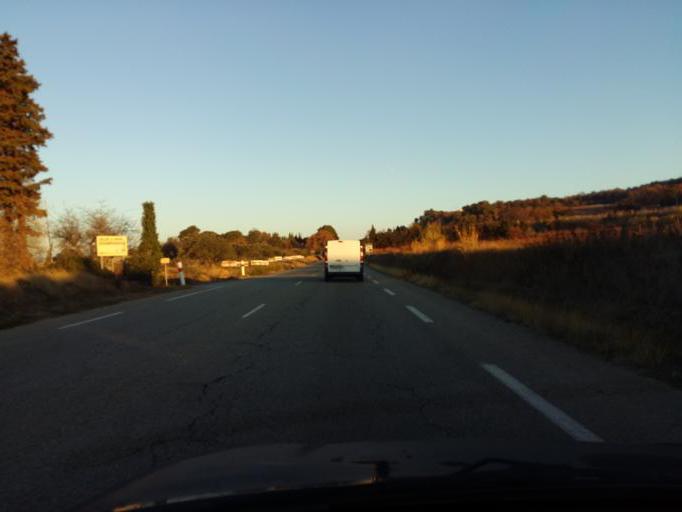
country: FR
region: Provence-Alpes-Cote d'Azur
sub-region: Departement du Vaucluse
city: Visan
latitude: 44.3222
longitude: 4.9471
